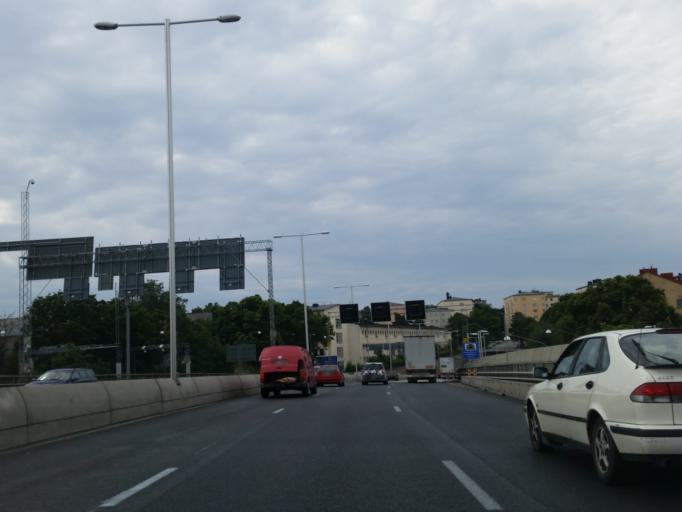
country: SE
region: Stockholm
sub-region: Solna Kommun
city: Solna
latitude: 59.3316
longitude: 18.0100
